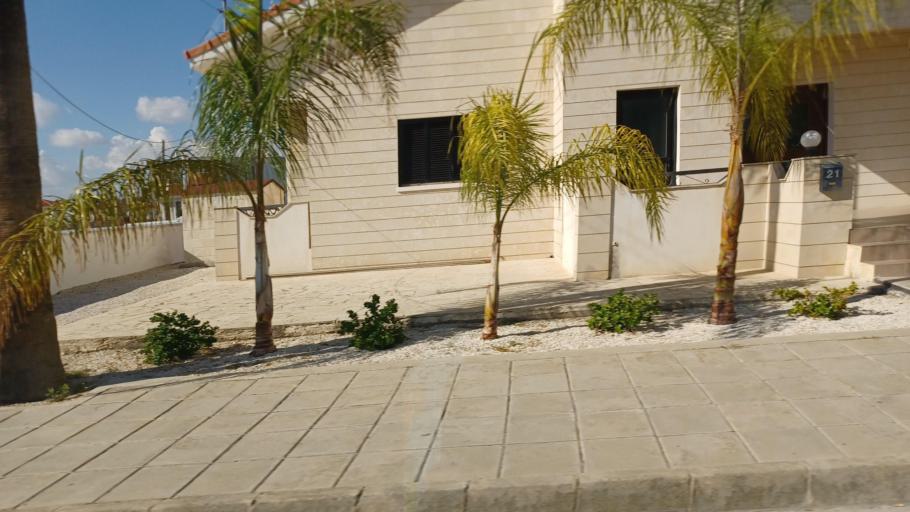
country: CY
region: Larnaka
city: Pyla
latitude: 34.9919
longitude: 33.6825
